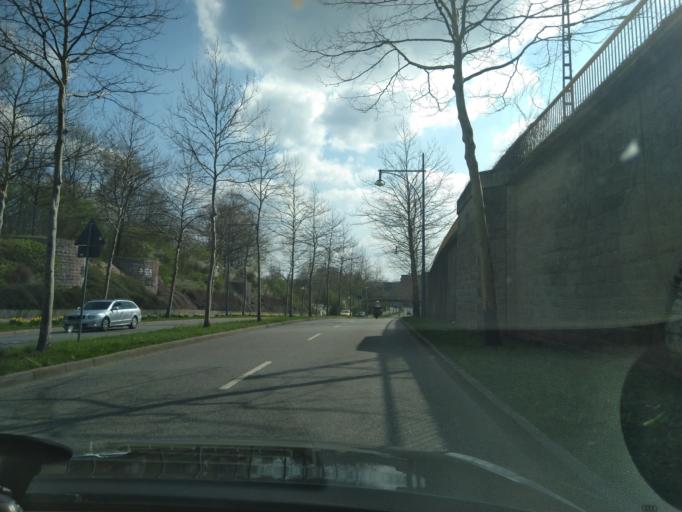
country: DE
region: Saxony
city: Chemnitz
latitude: 50.8265
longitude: 12.9152
